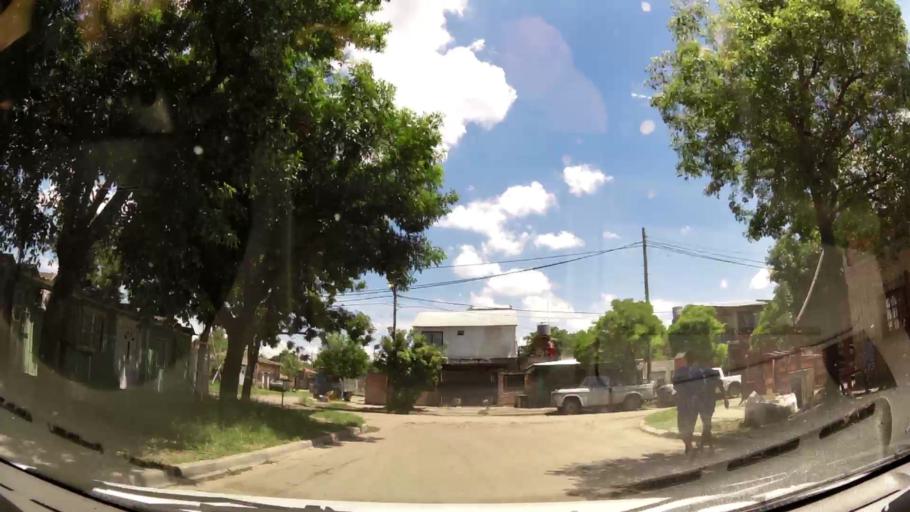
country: AR
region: Buenos Aires
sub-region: Partido de Merlo
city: Merlo
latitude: -34.6465
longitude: -58.6958
